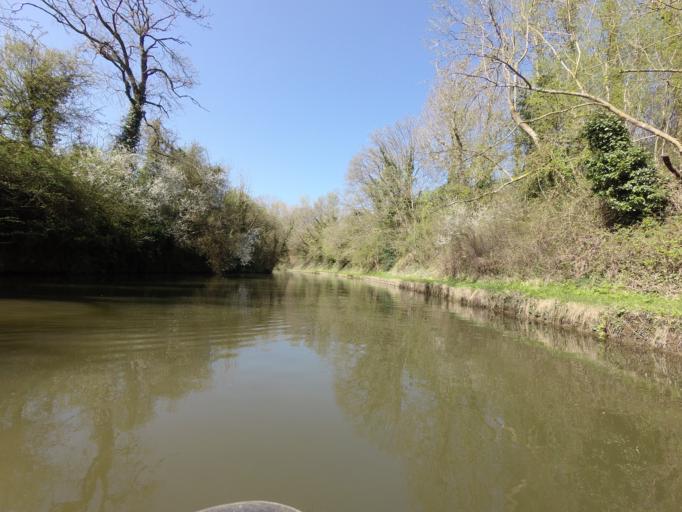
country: GB
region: England
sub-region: Hertfordshire
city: Tring
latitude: 51.7968
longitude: -0.6201
